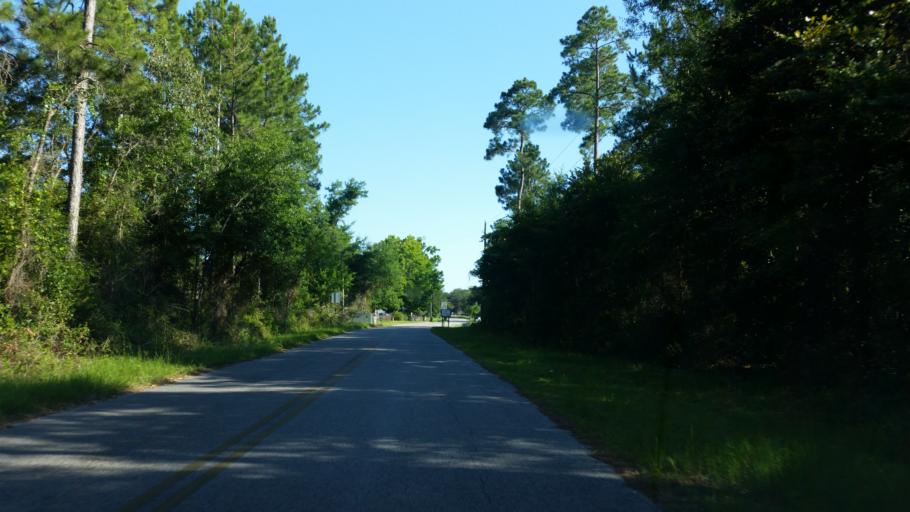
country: US
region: Florida
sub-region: Escambia County
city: Bellview
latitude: 30.4636
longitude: -87.4094
